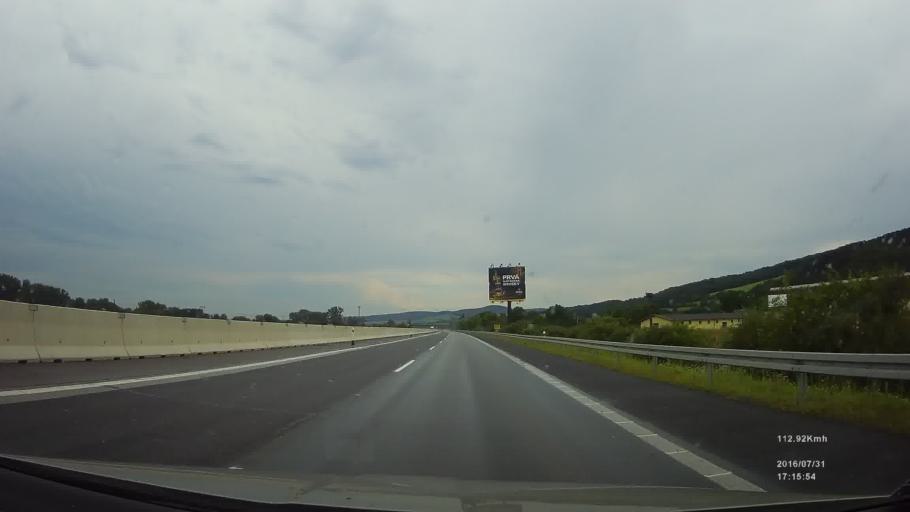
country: SK
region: Presovsky
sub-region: Okres Presov
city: Presov
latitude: 48.9005
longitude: 21.2487
